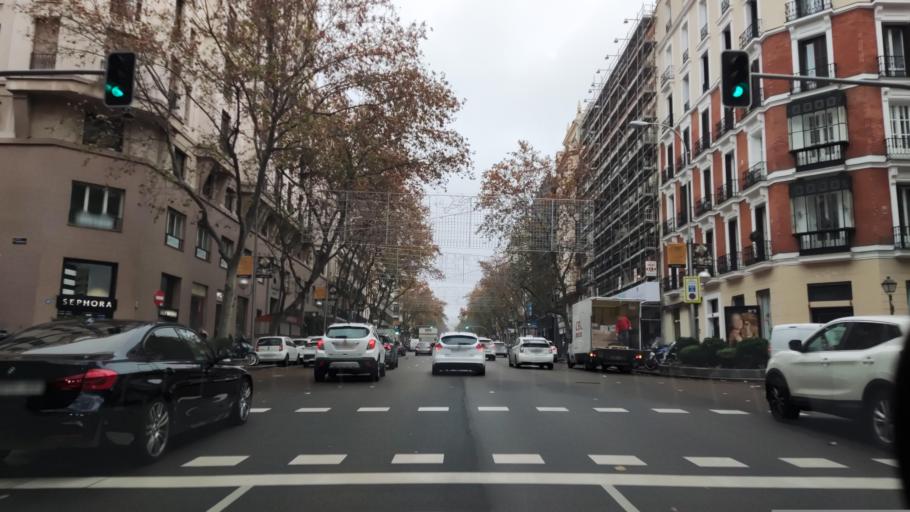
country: ES
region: Madrid
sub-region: Provincia de Madrid
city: Salamanca
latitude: 40.4261
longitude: -3.6841
